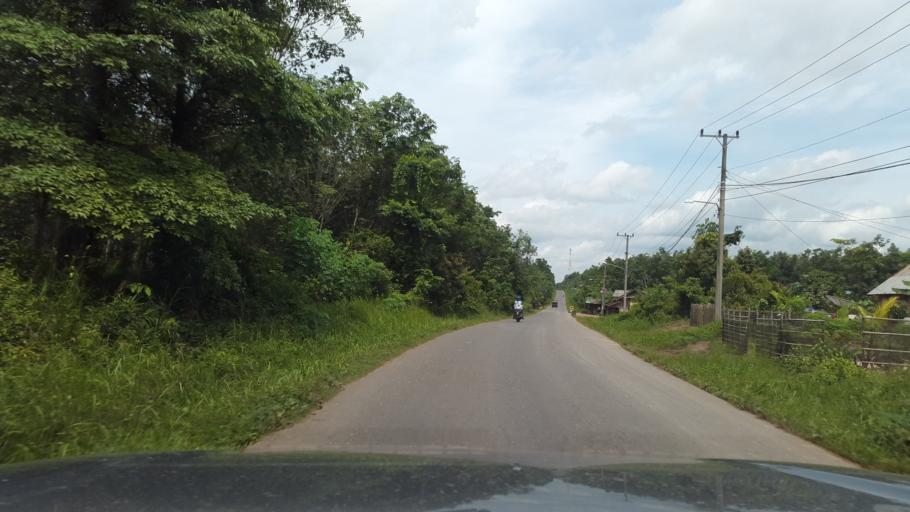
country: ID
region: South Sumatra
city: Gunungmegang Dalam
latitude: -3.3959
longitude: 103.9596
